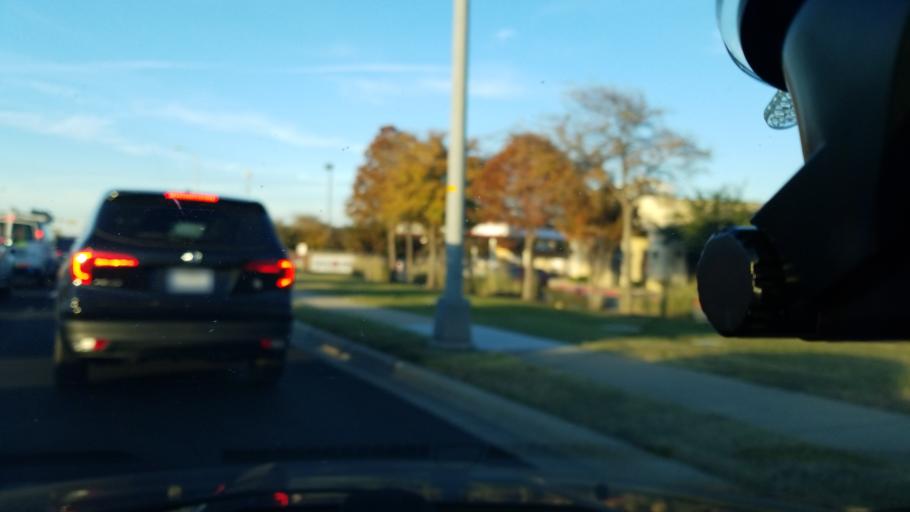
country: US
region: Texas
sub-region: Williamson County
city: Round Rock
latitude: 30.4948
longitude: -97.6563
